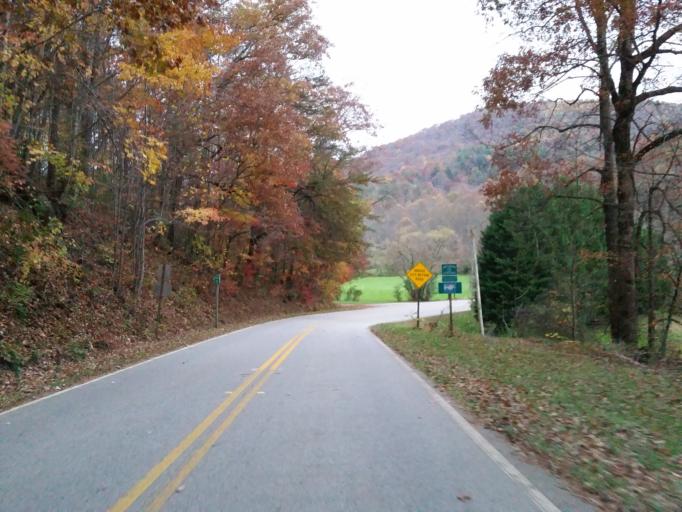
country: US
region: Georgia
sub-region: Lumpkin County
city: Dahlonega
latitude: 34.7046
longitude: -84.0568
